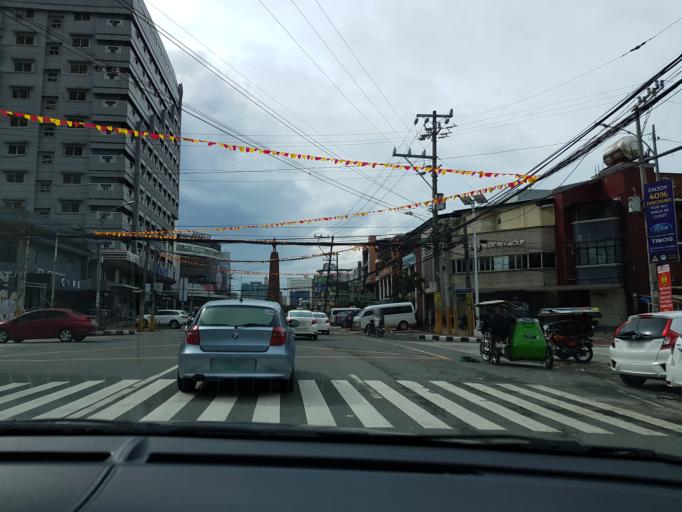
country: PH
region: Calabarzon
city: Del Monte
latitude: 14.6360
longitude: 121.0356
